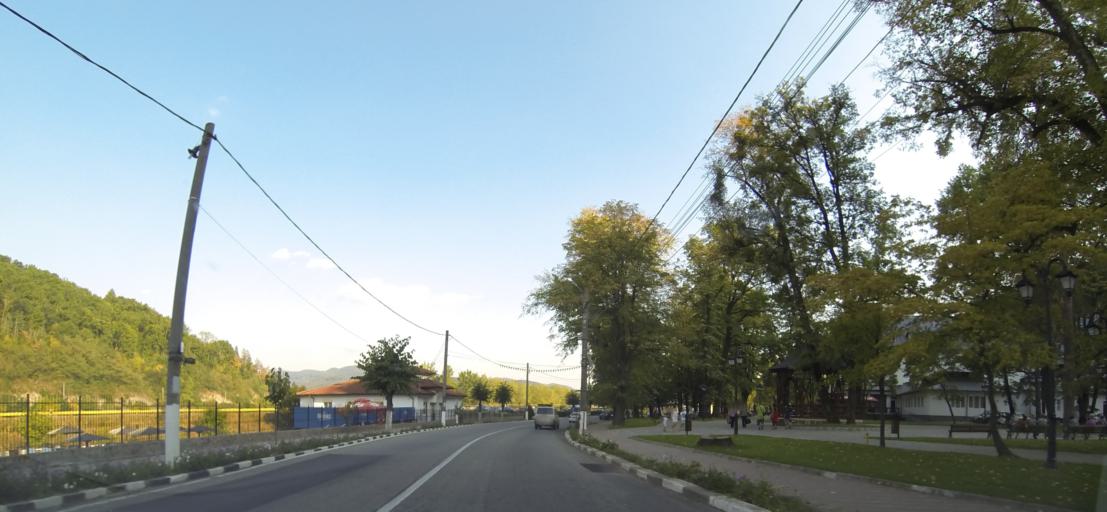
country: RO
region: Valcea
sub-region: Oras Calimanesti
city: Jiblea Veche
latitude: 45.2491
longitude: 24.3377
